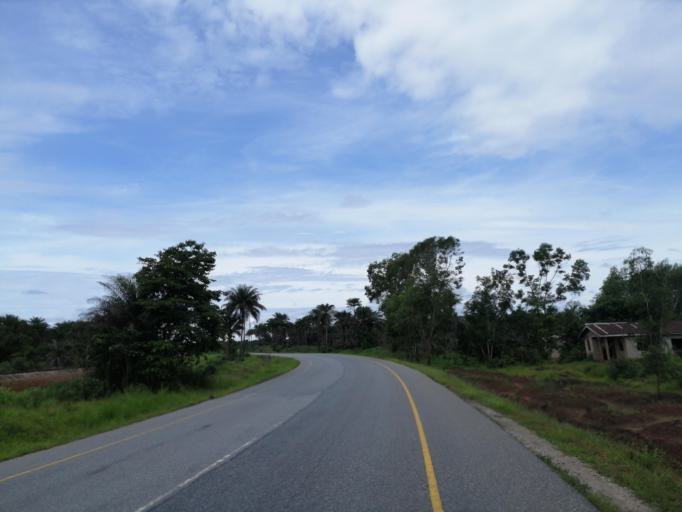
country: SL
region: Northern Province
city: Port Loko
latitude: 8.7542
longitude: -12.9169
